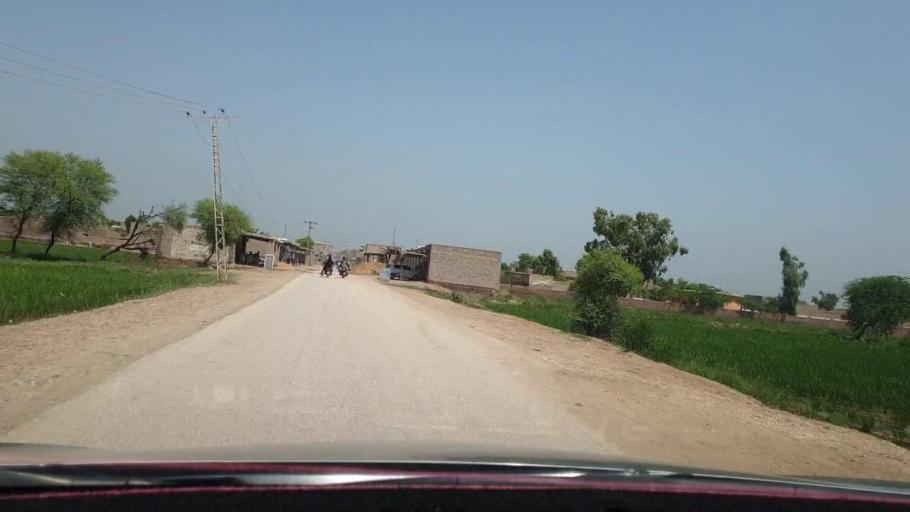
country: PK
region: Sindh
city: Warah
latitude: 27.4456
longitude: 67.7909
